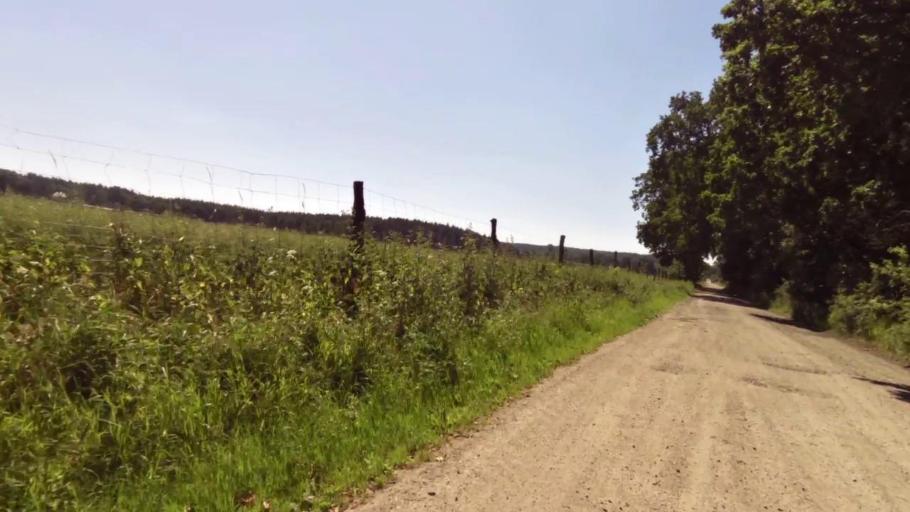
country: PL
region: West Pomeranian Voivodeship
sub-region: Powiat swidwinski
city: Rabino
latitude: 53.8947
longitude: 16.0097
